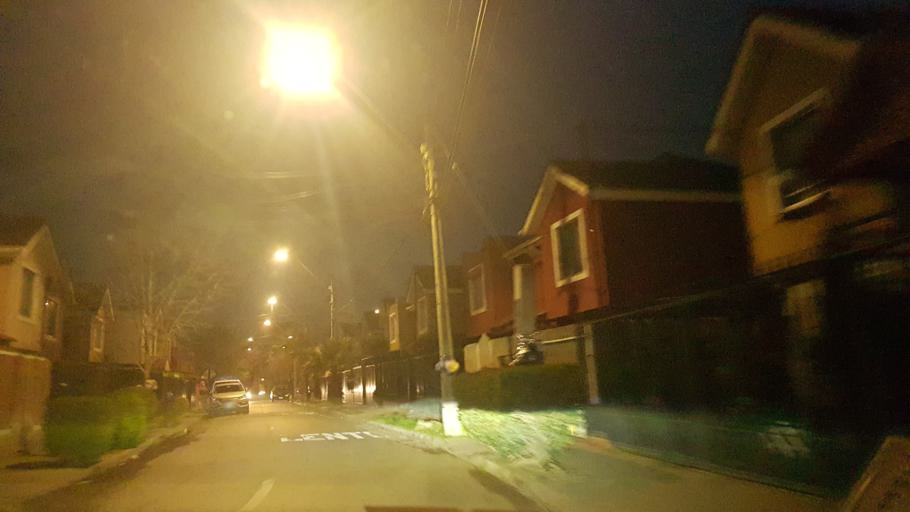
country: CL
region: Santiago Metropolitan
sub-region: Provincia de Santiago
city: Lo Prado
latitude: -33.3586
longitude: -70.7183
